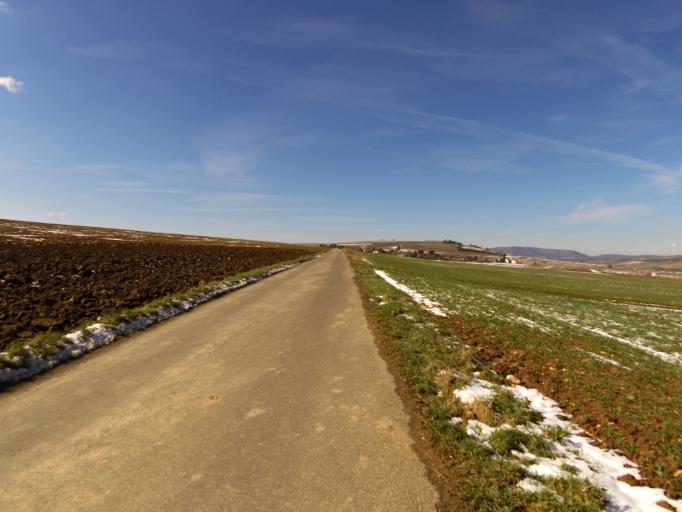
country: DE
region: Rheinland-Pfalz
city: Bubenheim
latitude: 49.6401
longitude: 8.1191
